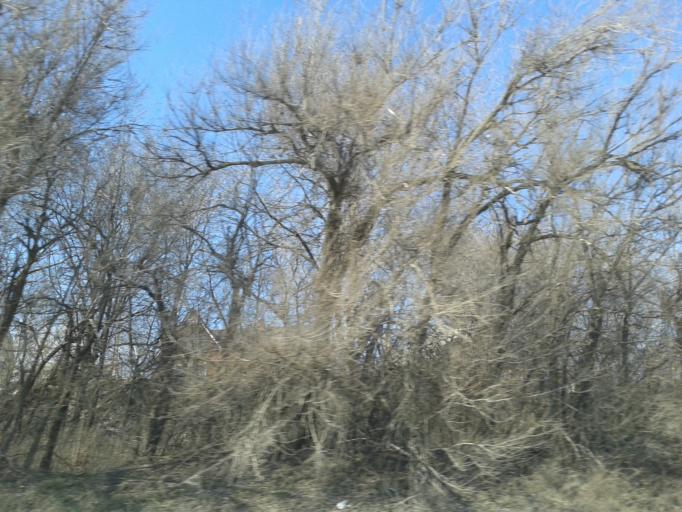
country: RU
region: Volgograd
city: Volgograd
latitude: 48.6303
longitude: 44.4024
